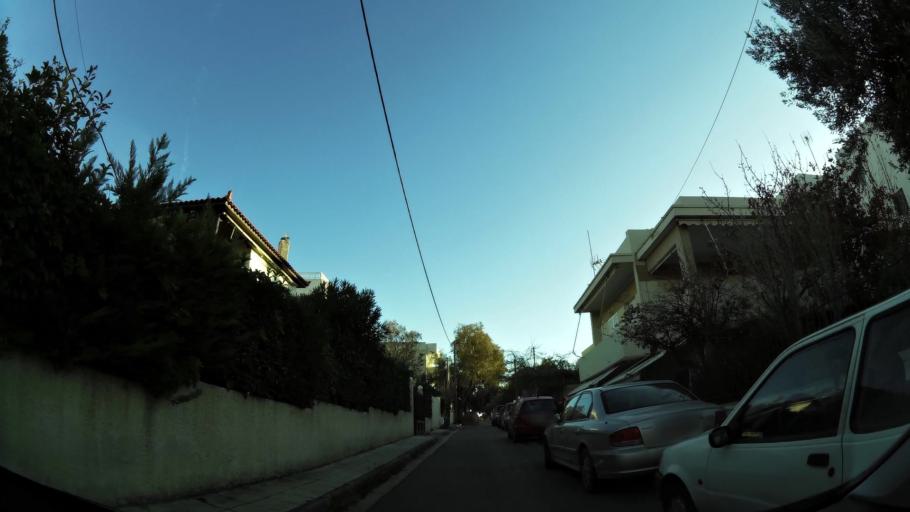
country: GR
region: Attica
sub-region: Nomarchia Anatolikis Attikis
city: Rafina
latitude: 38.0160
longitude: 24.0129
